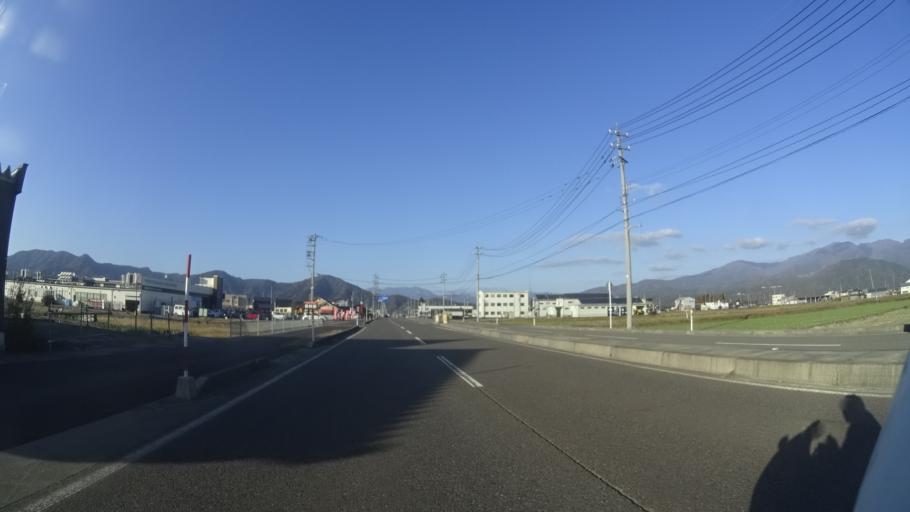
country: JP
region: Fukui
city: Ono
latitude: 35.9856
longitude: 136.5103
